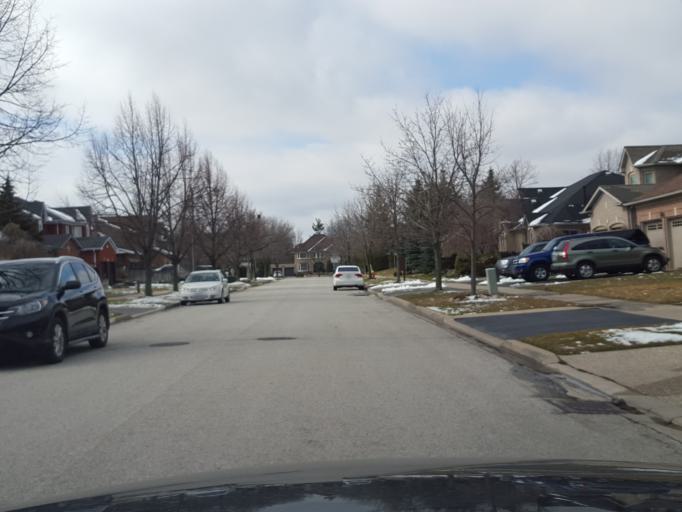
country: CA
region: Ontario
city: Burlington
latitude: 43.3869
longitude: -79.8015
